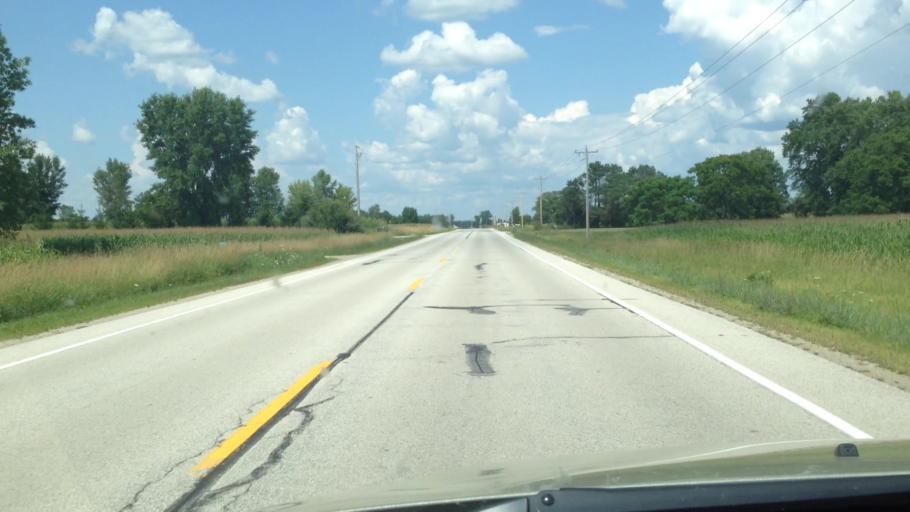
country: US
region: Wisconsin
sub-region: Brown County
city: Pulaski
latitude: 44.6486
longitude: -88.1808
